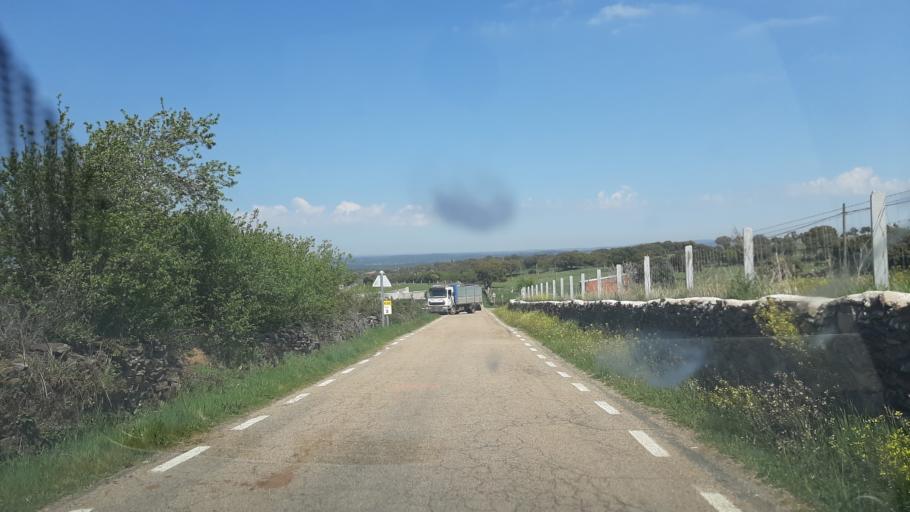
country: ES
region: Castille and Leon
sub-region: Provincia de Salamanca
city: Navarredonda de la Rinconada
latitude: 40.6146
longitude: -6.0194
